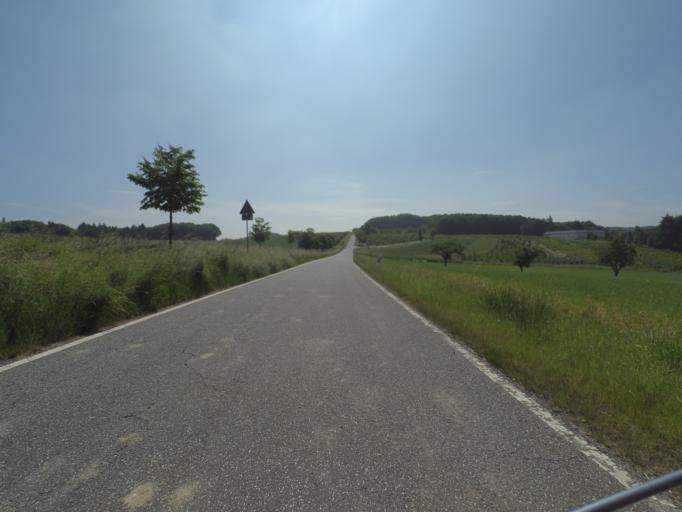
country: DE
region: Rheinland-Pfalz
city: Nortershausen
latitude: 50.2146
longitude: 7.4625
